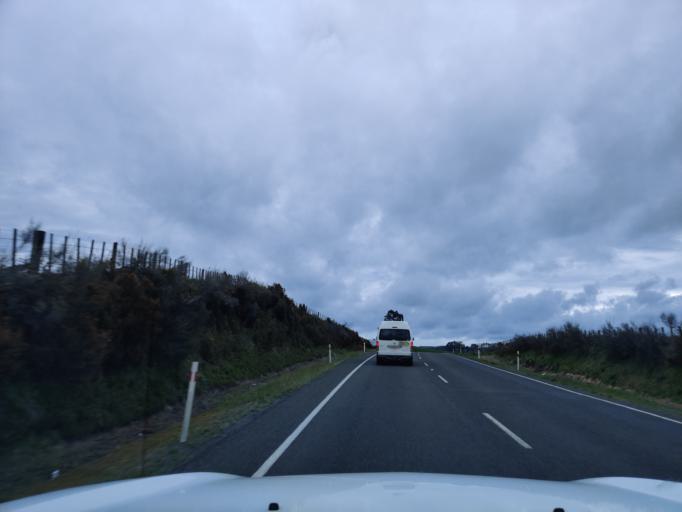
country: NZ
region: Waikato
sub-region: Otorohanga District
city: Otorohanga
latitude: -38.4554
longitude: 175.1662
